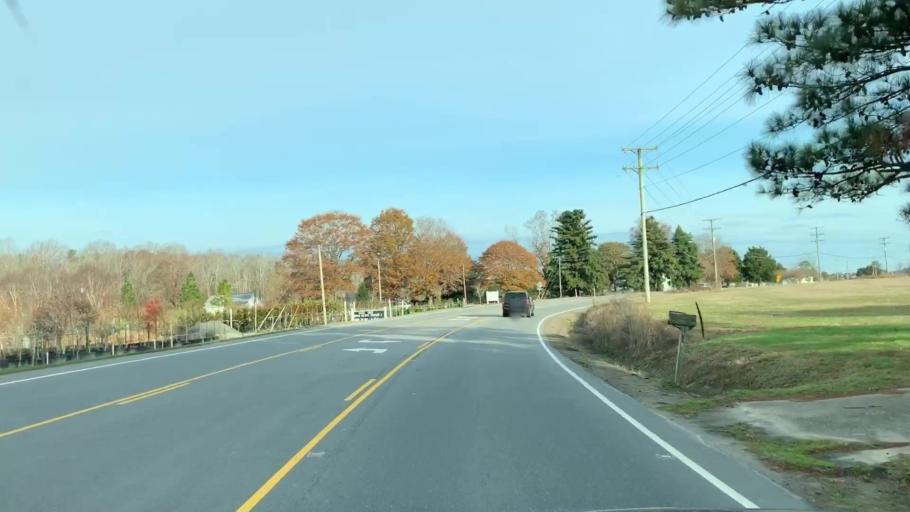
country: US
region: Virginia
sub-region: City of Virginia Beach
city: Virginia Beach
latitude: 36.6912
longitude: -76.0254
